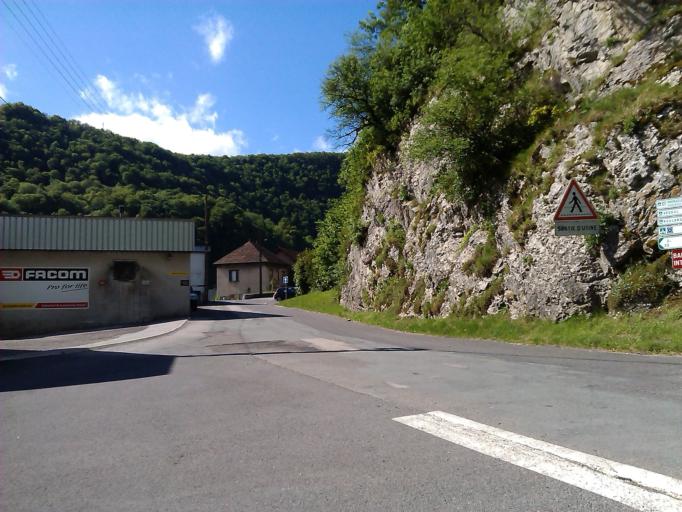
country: FR
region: Franche-Comte
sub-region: Departement du Doubs
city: Roulans
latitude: 47.3010
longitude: 6.2354
